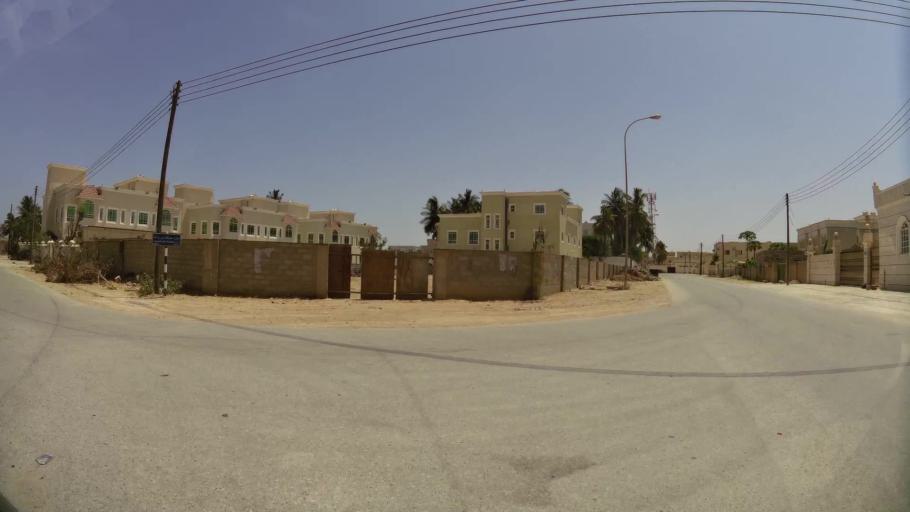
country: OM
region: Zufar
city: Salalah
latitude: 17.0580
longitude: 54.1579
